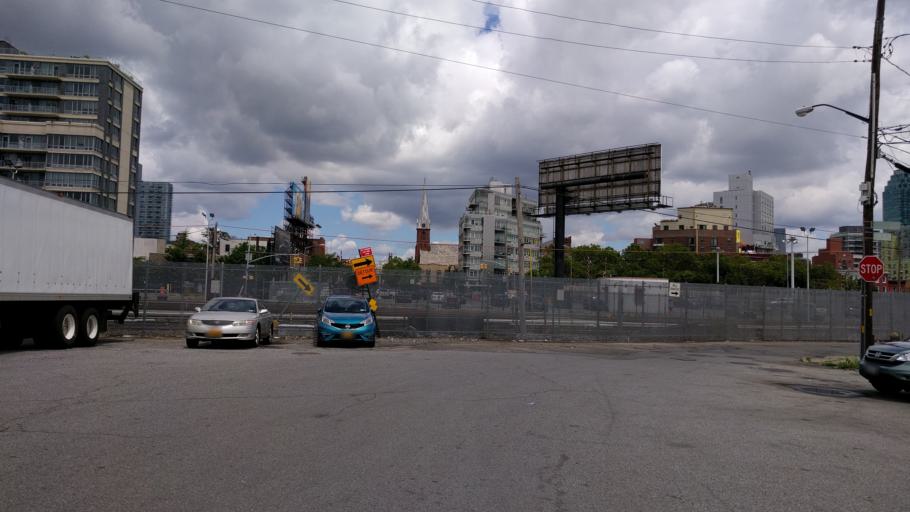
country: US
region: New York
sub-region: Queens County
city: Long Island City
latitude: 40.7404
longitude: -73.9548
